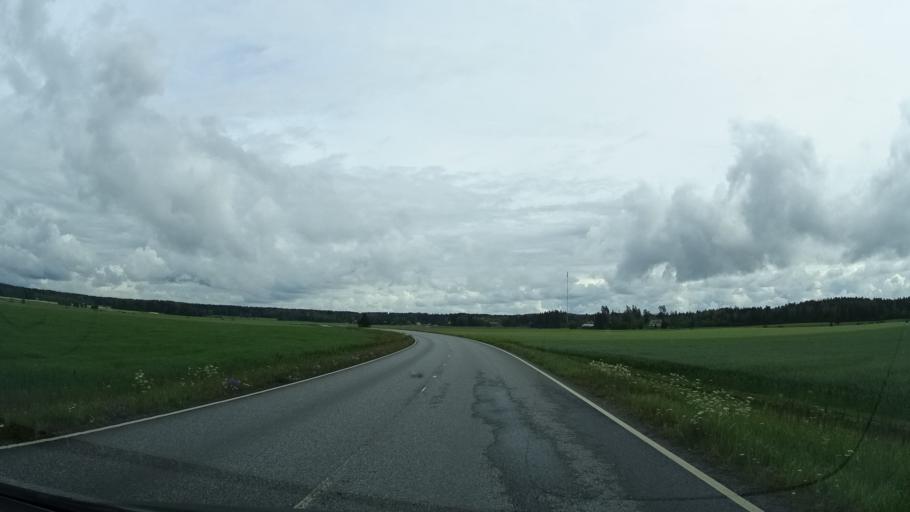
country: FI
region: Haeme
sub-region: Forssa
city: Humppila
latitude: 61.0996
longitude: 23.2966
